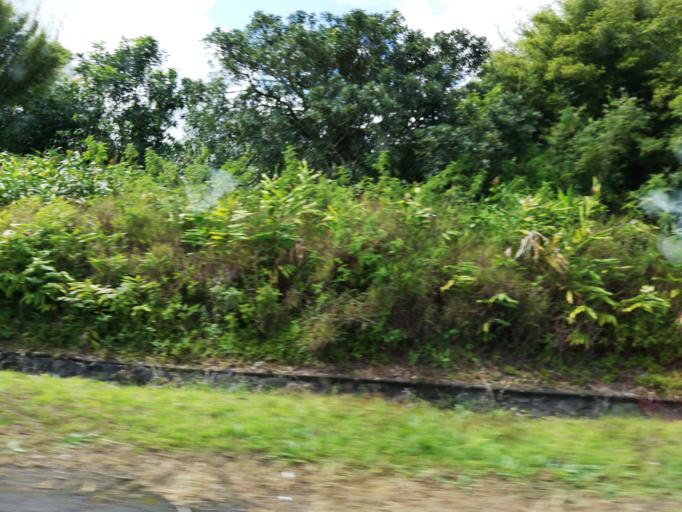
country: MU
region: Plaines Wilhems
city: Midlands
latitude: -20.3186
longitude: 57.5418
